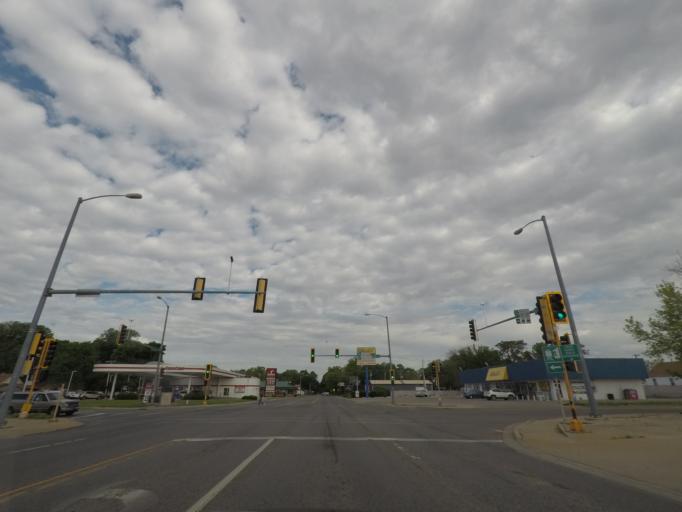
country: US
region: Illinois
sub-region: Logan County
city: Lincoln
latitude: 40.1531
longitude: -89.3595
